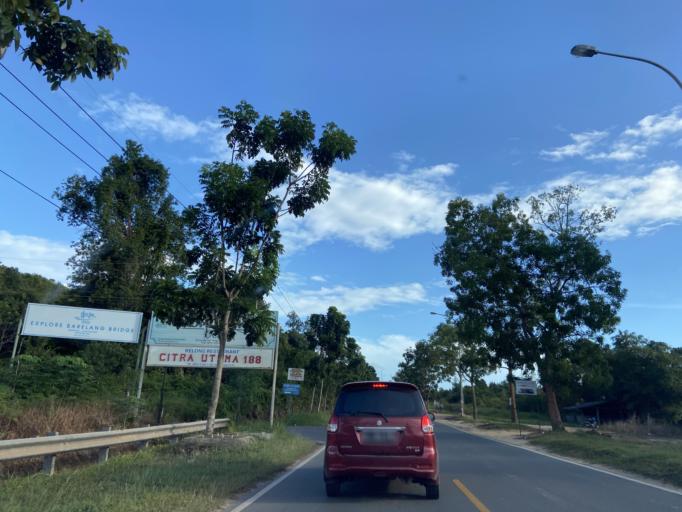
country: SG
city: Singapore
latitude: 0.9926
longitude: 104.0344
